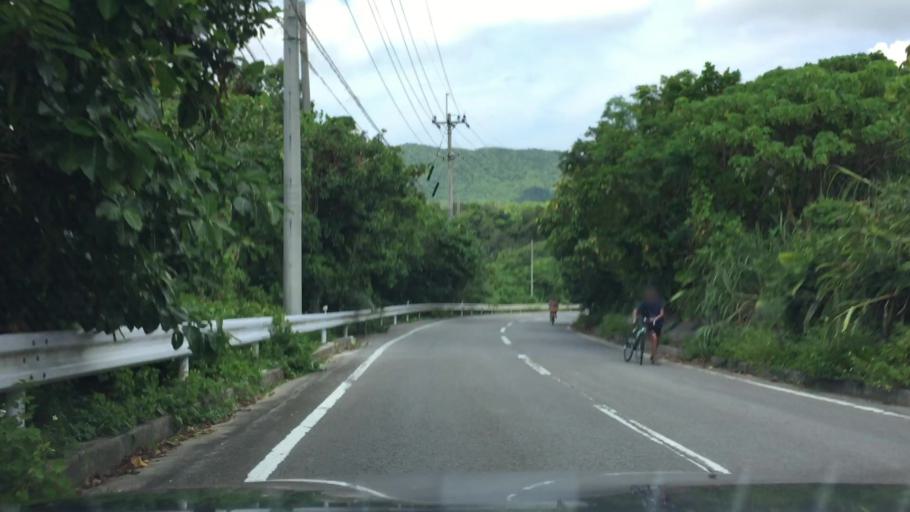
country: JP
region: Okinawa
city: Ishigaki
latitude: 24.4545
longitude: 124.2081
